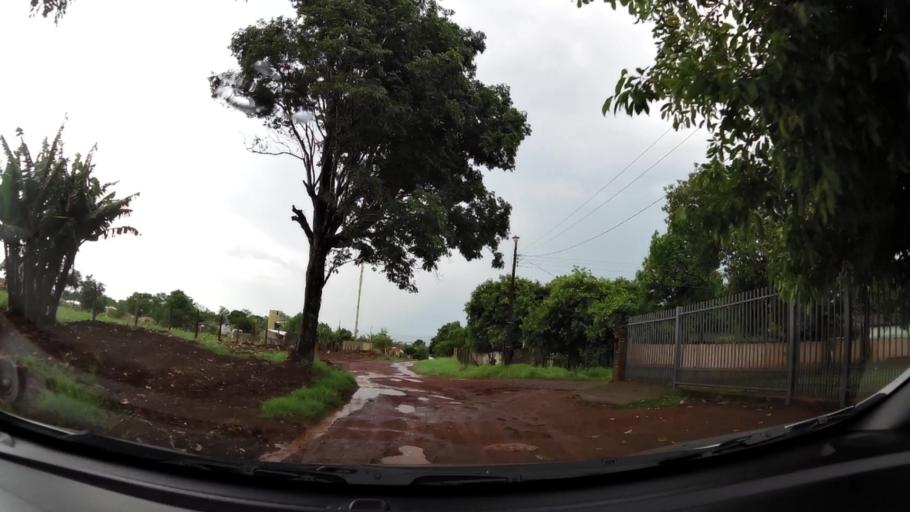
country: PY
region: Alto Parana
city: Presidente Franco
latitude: -25.5452
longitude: -54.6489
